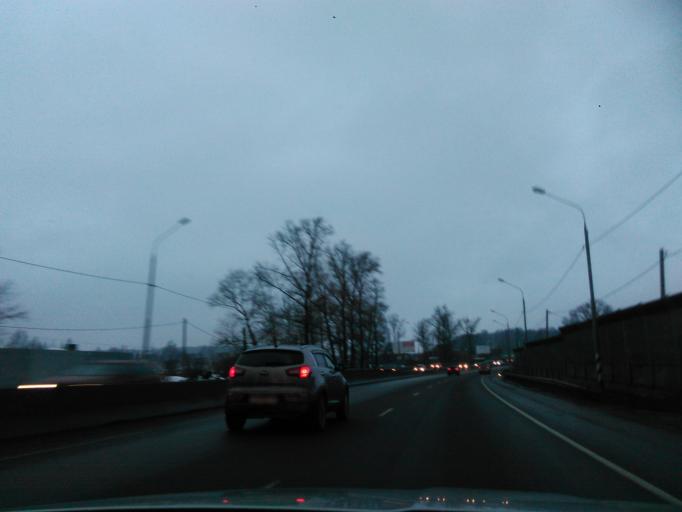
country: RU
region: Moskovskaya
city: Chashnikovo
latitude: 56.0313
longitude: 37.1657
